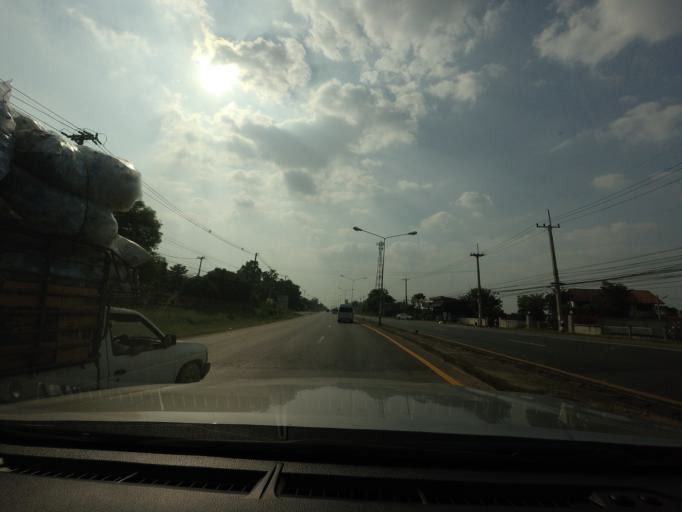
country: TH
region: Sukhothai
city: Sukhothai
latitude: 17.0260
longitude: 99.8798
